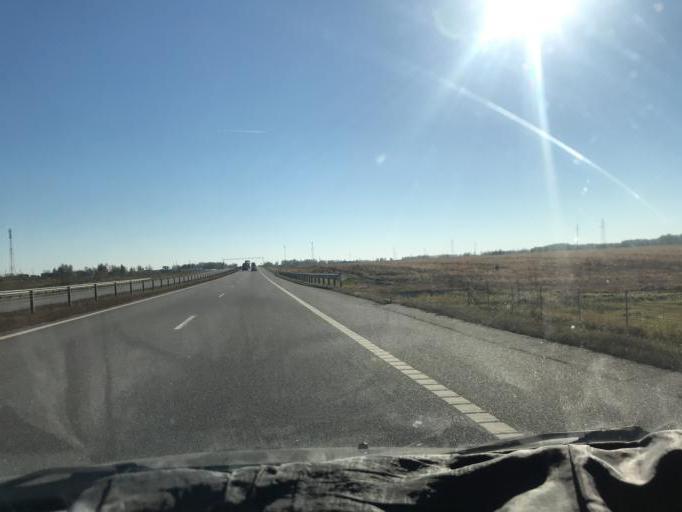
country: BY
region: Mogilev
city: Yalizava
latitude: 53.2562
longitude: 28.9094
